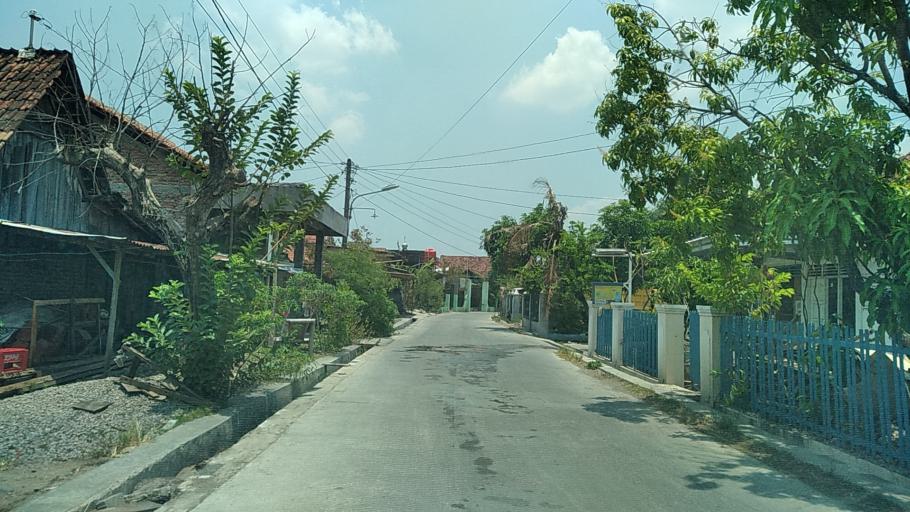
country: ID
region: Central Java
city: Mranggen
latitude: -7.0137
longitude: 110.4893
